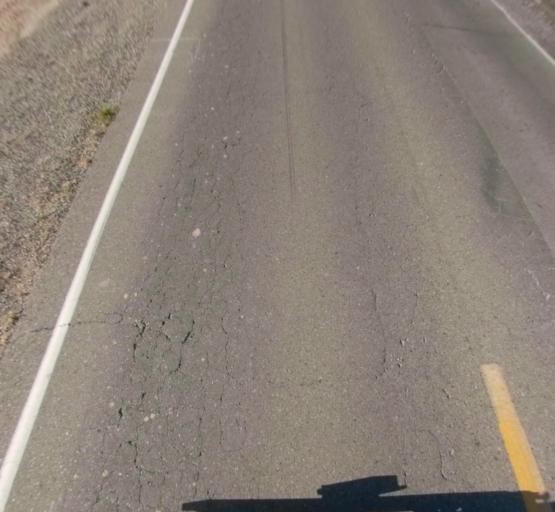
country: US
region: California
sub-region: Madera County
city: Madera
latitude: 36.9468
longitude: -120.1283
